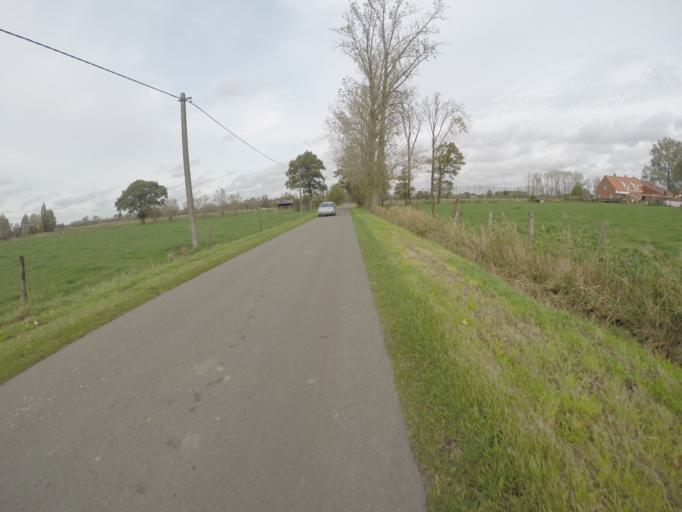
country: BE
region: Flanders
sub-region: Provincie Oost-Vlaanderen
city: Maldegem
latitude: 51.1795
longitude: 3.4281
